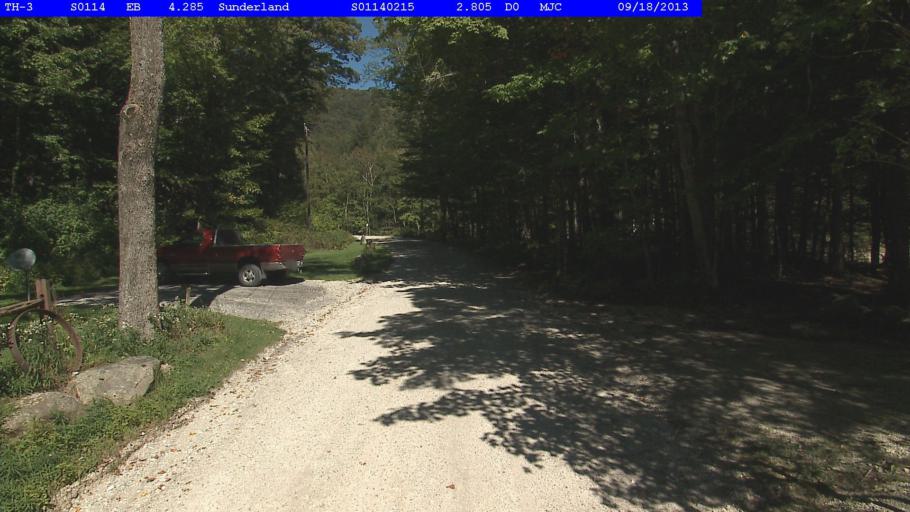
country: US
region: Vermont
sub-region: Bennington County
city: Arlington
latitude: 43.0406
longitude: -73.1038
